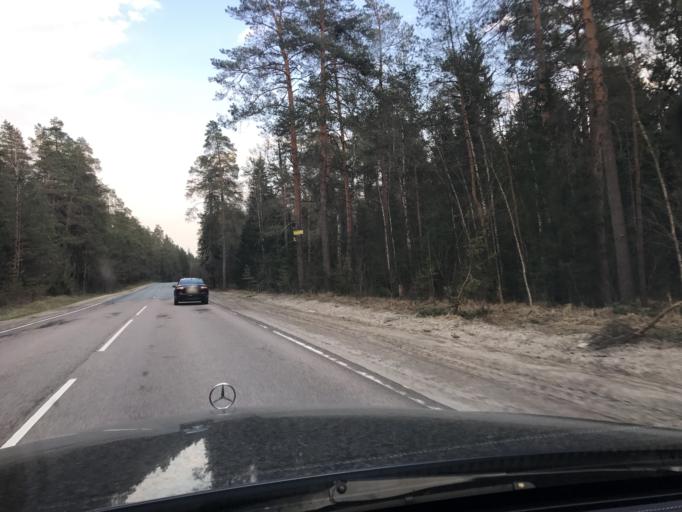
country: RU
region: Vladimir
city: Muromtsevo
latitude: 55.9580
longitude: 40.9821
